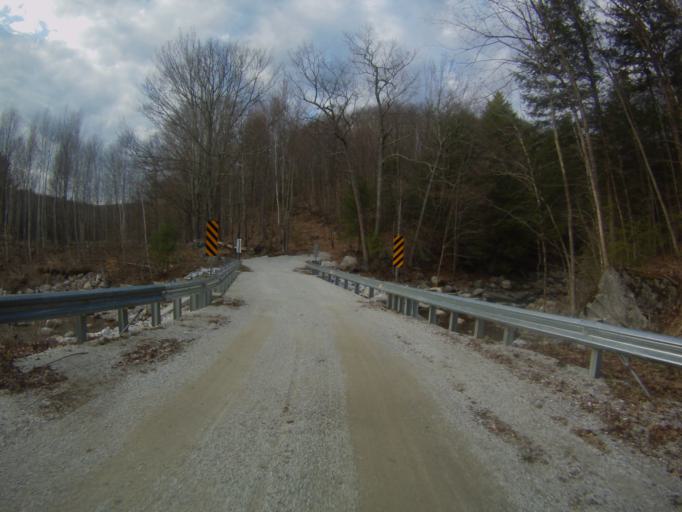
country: US
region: Vermont
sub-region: Rutland County
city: Brandon
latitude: 43.8383
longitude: -73.0406
